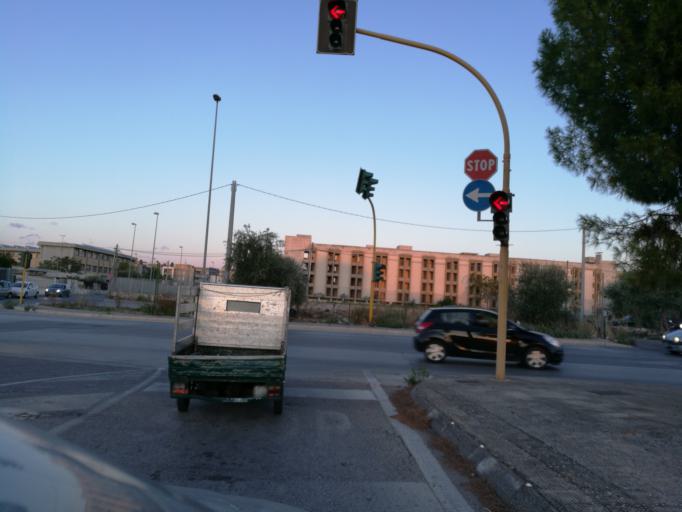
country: IT
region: Apulia
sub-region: Provincia di Bari
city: Loseto
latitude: 41.0674
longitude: 16.8626
